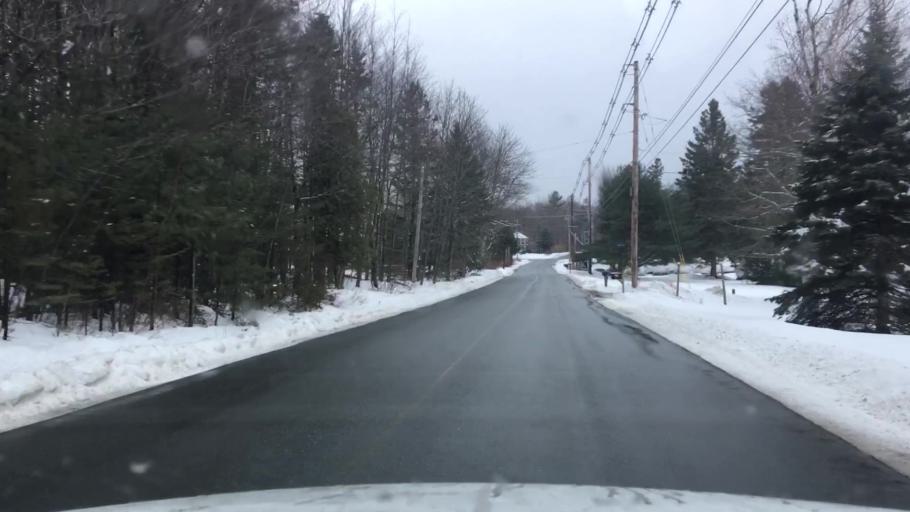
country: US
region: Maine
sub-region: Hancock County
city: Trenton
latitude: 44.4134
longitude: -68.3345
